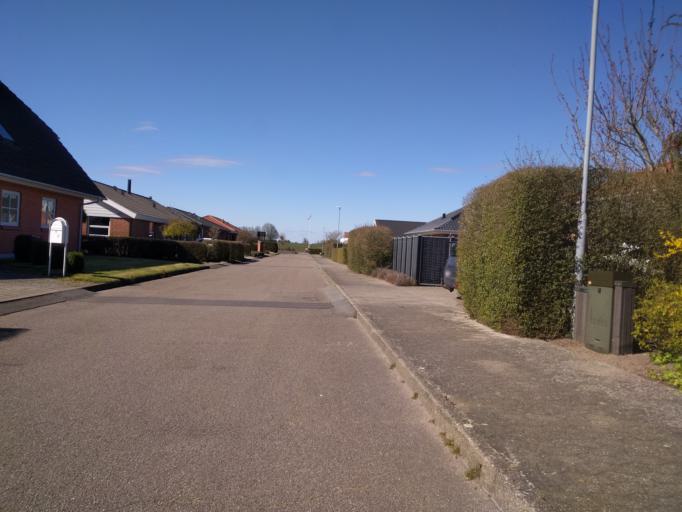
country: DK
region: South Denmark
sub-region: Kerteminde Kommune
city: Langeskov
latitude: 55.3653
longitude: 10.5903
